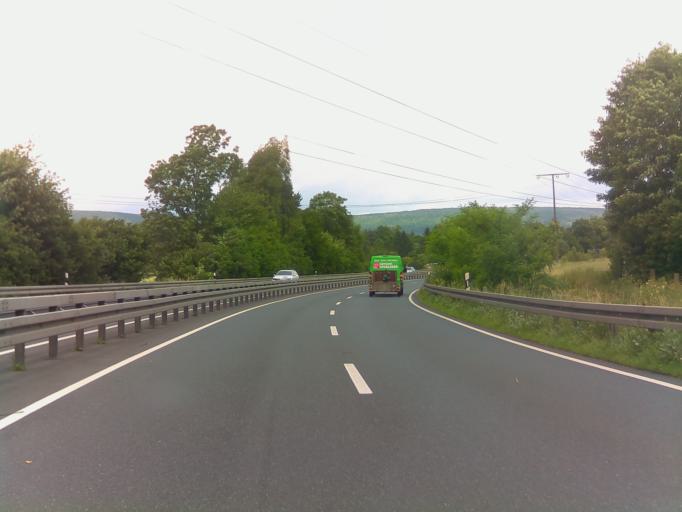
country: DE
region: Lower Saxony
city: Springe
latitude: 52.1985
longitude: 9.5301
